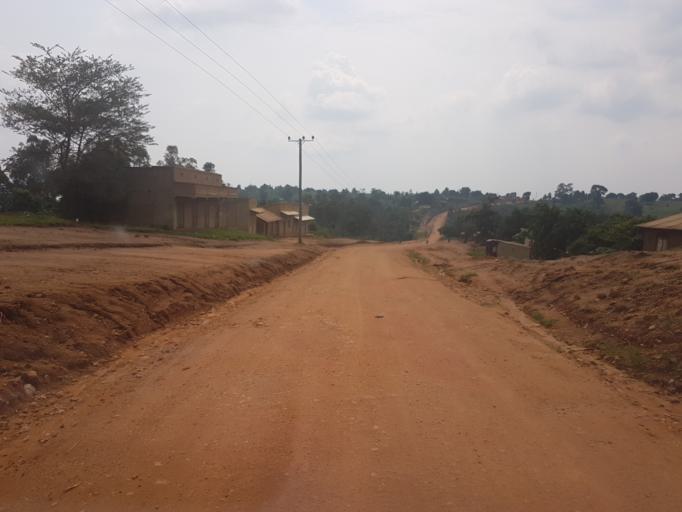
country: UG
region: Western Region
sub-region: Kanungu District
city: Ntungamo
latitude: -0.8207
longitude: 29.7081
